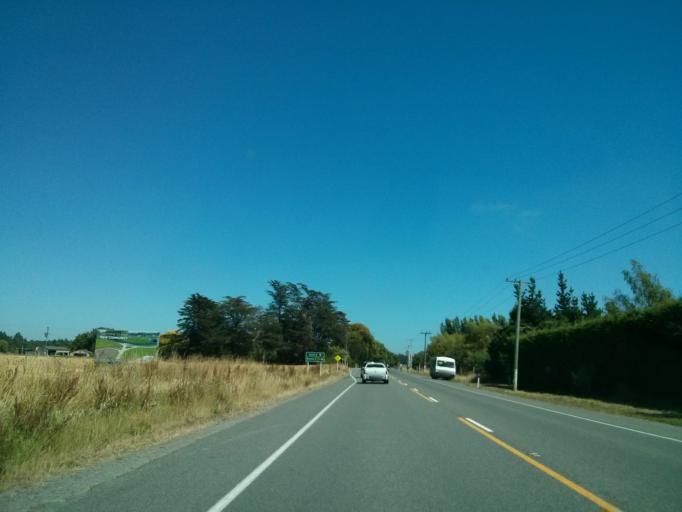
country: NZ
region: Canterbury
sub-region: Waimakariri District
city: Kaiapoi
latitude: -43.4065
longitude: 172.6304
